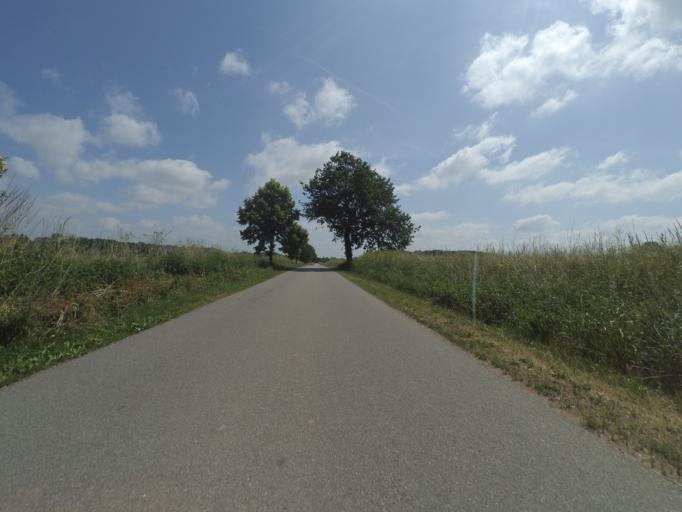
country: DE
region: Mecklenburg-Vorpommern
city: Siggelkow
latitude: 53.4164
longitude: 11.9713
